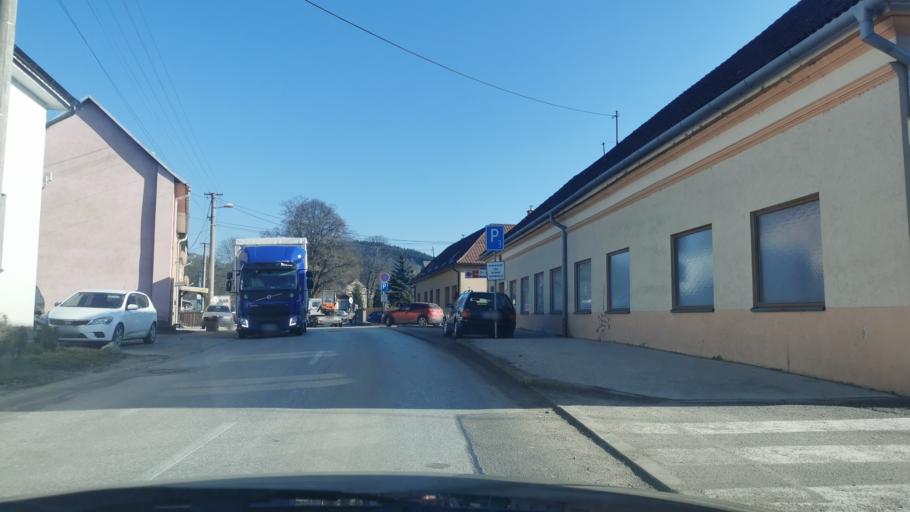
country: SK
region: Trenciansky
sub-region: Okres Myjava
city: Myjava
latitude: 48.7446
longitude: 17.5358
